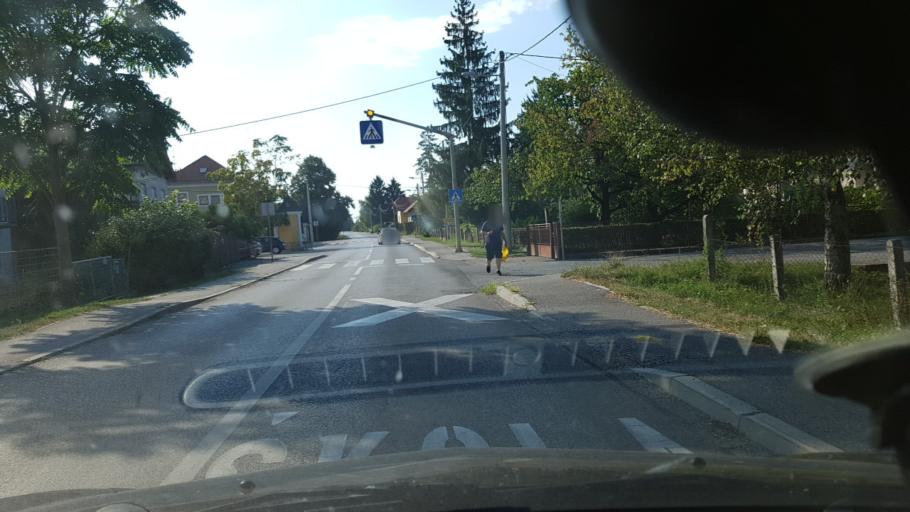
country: HR
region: Zagrebacka
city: Bregana
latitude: 45.8875
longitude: 15.6963
